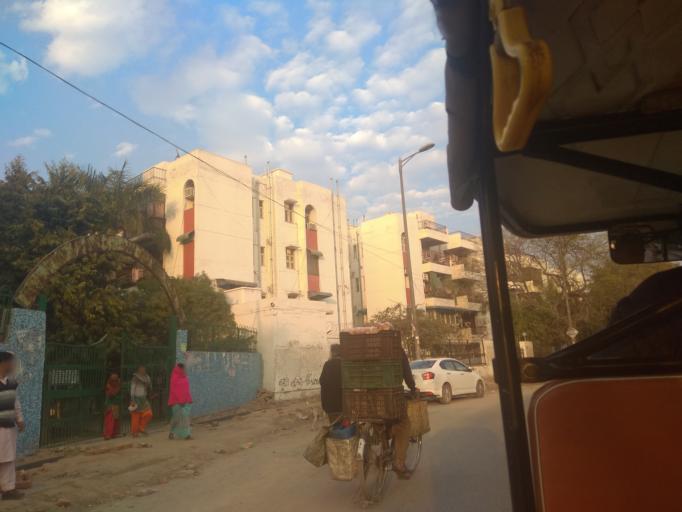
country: IN
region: NCT
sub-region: West Delhi
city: Nangloi Jat
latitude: 28.6355
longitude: 77.0643
